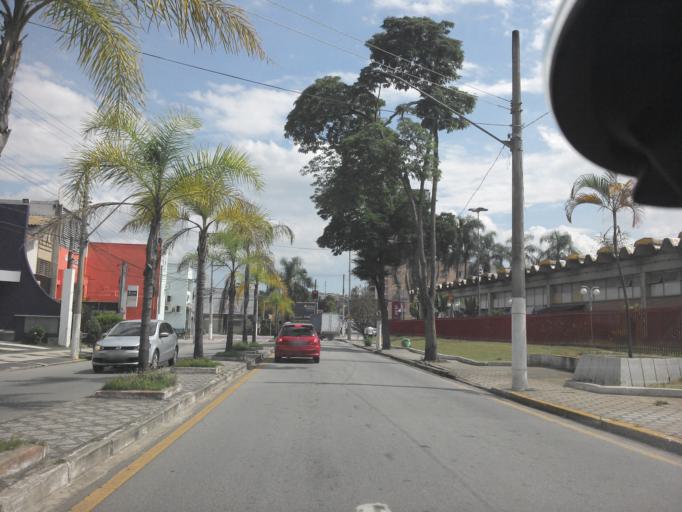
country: BR
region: Sao Paulo
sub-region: Taubate
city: Taubate
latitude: -23.0367
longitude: -45.5793
